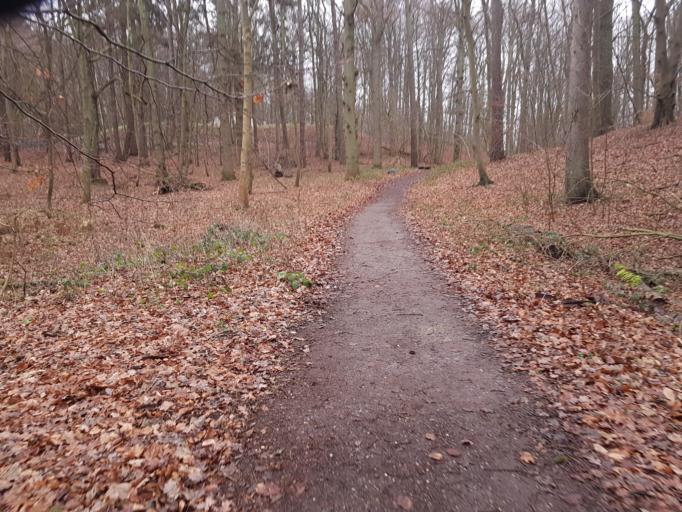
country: DE
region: Mecklenburg-Vorpommern
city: Ostseebad Binz
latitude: 54.3951
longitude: 13.6180
